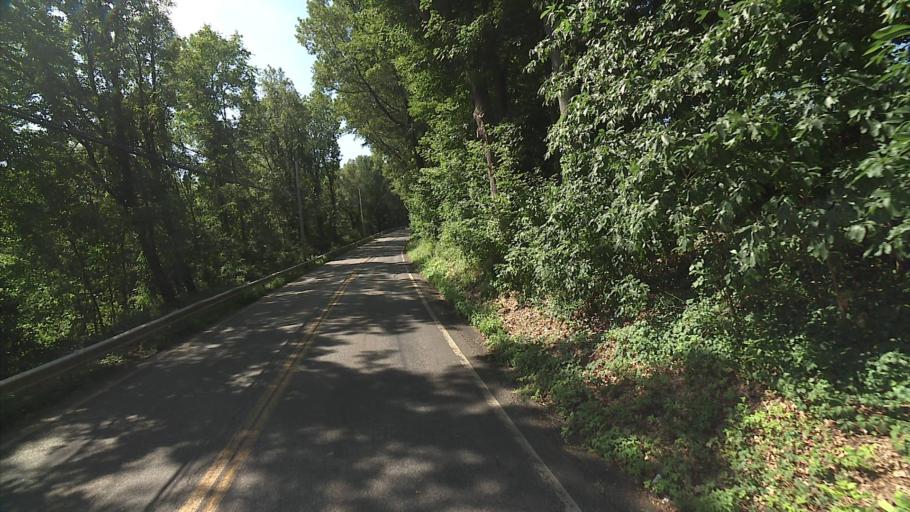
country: US
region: Connecticut
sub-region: Tolland County
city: Stafford
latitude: 41.9506
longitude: -72.1911
